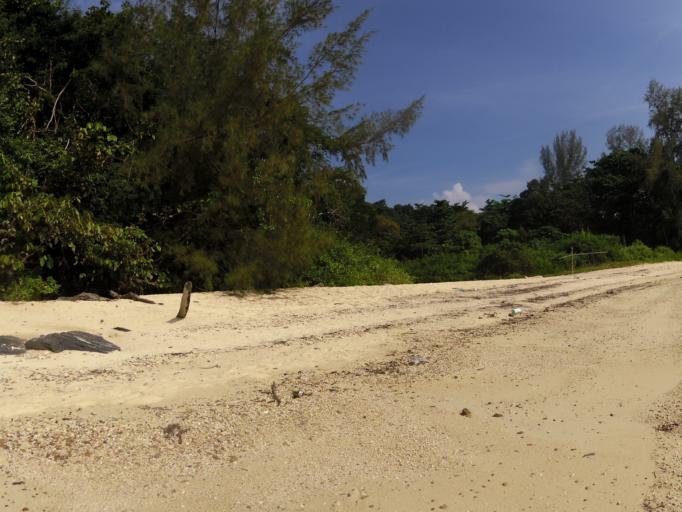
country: MY
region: Kedah
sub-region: Langkawi
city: Kuah
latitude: 6.2199
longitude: 99.7198
